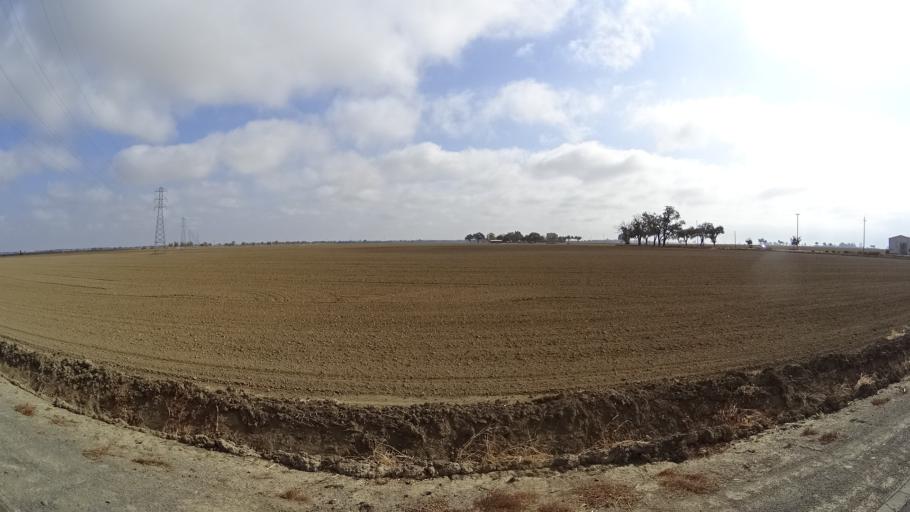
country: US
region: California
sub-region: Yolo County
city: Woodland
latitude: 38.7944
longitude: -121.7750
